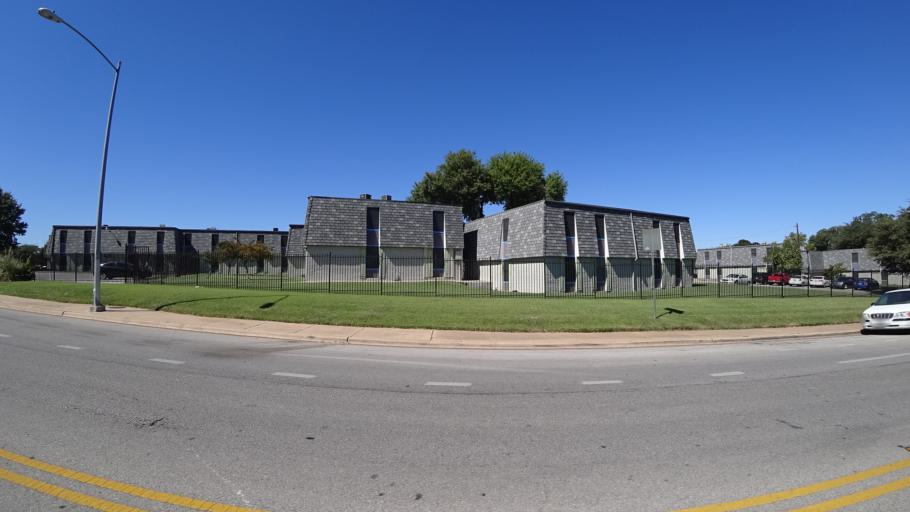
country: US
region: Texas
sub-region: Travis County
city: Austin
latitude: 30.2201
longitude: -97.7429
